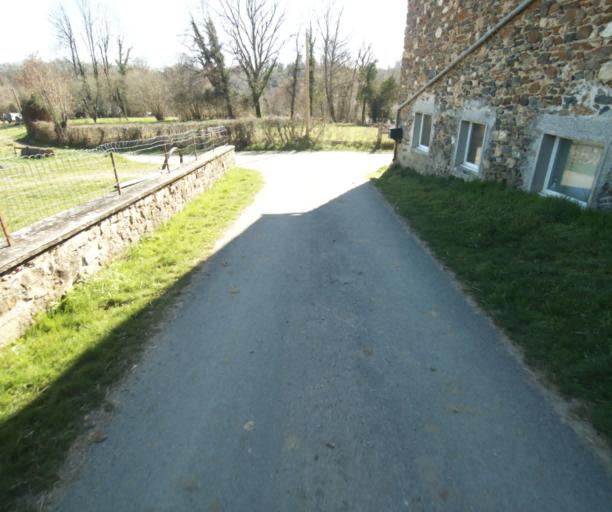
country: FR
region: Limousin
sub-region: Departement de la Correze
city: Chamboulive
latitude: 45.4331
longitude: 1.6487
